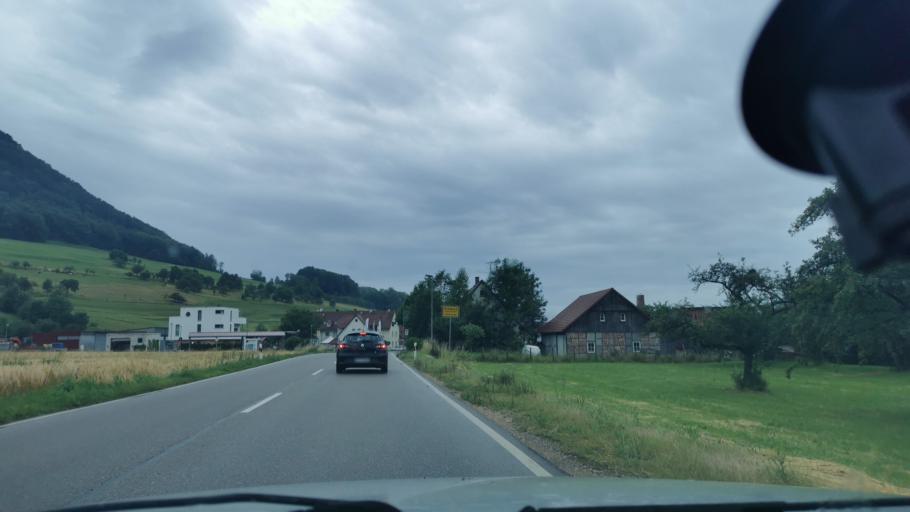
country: DE
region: Baden-Wuerttemberg
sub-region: Regierungsbezirk Stuttgart
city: Donzdorf
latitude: 48.7009
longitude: 9.8395
